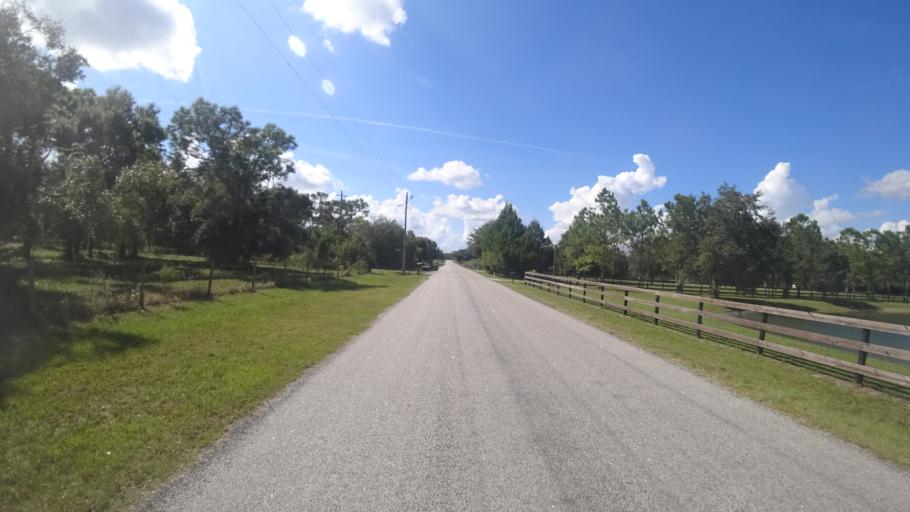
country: US
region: Florida
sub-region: Sarasota County
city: The Meadows
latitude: 27.4671
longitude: -82.2944
